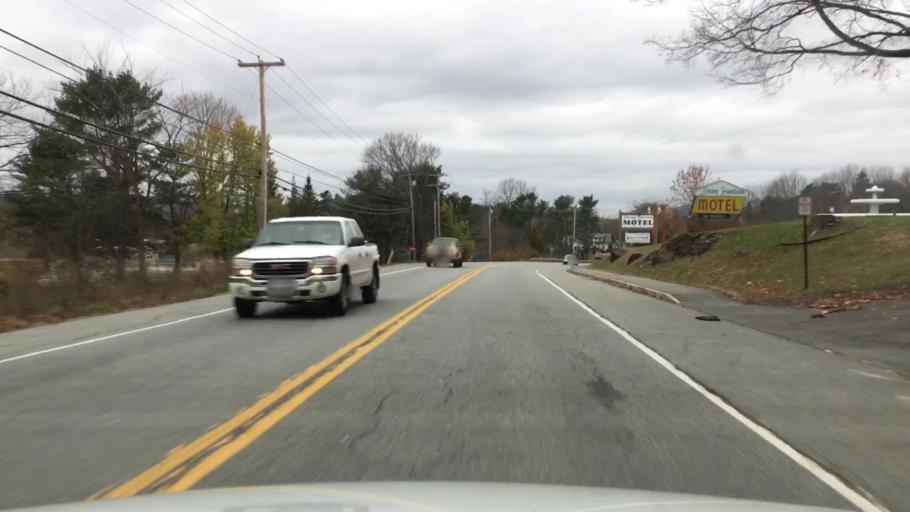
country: US
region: Maine
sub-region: Hancock County
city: Bucksport
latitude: 44.5694
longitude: -68.7709
